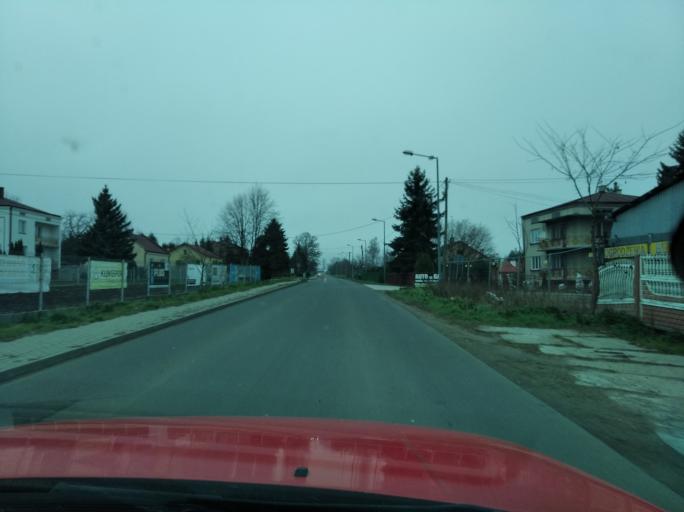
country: PL
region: Subcarpathian Voivodeship
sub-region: Powiat jaroslawski
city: Pawlosiow
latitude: 50.0115
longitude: 22.6502
